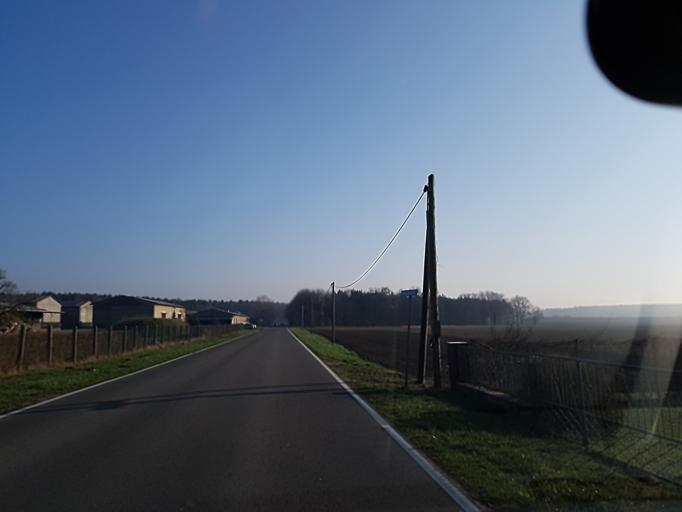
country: DE
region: Brandenburg
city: Bronkow
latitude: 51.6551
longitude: 13.8983
